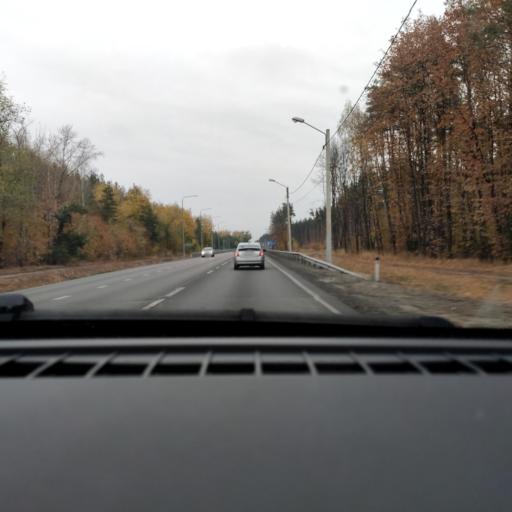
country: RU
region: Voronezj
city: Somovo
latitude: 51.6890
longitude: 39.2955
